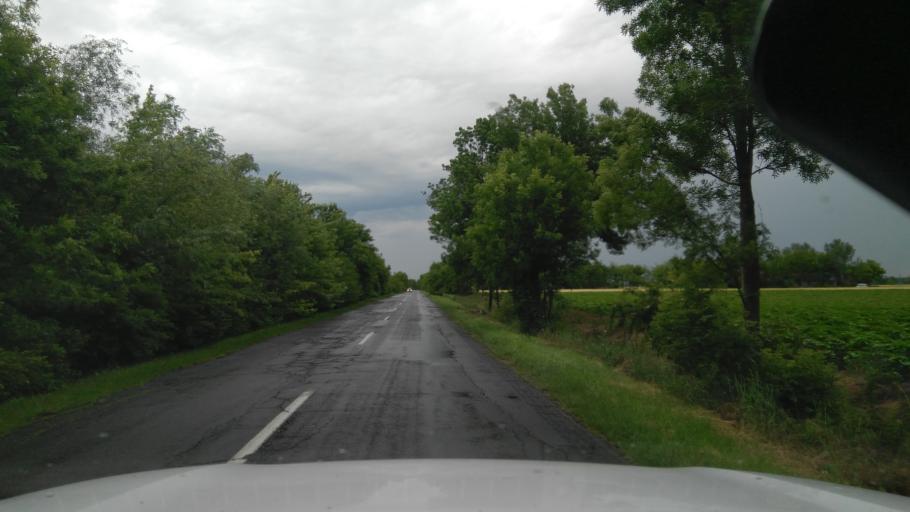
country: HU
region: Bekes
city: Bekescsaba
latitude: 46.6865
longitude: 21.1670
